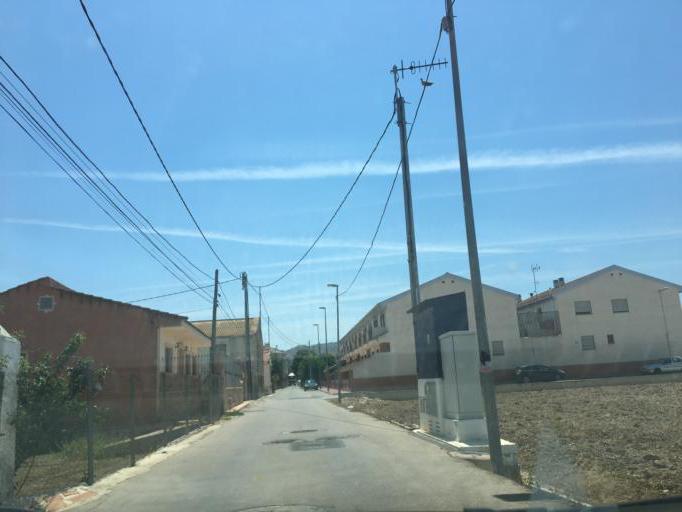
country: ES
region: Murcia
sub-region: Murcia
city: Santomera
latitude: 38.0176
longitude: -1.0550
